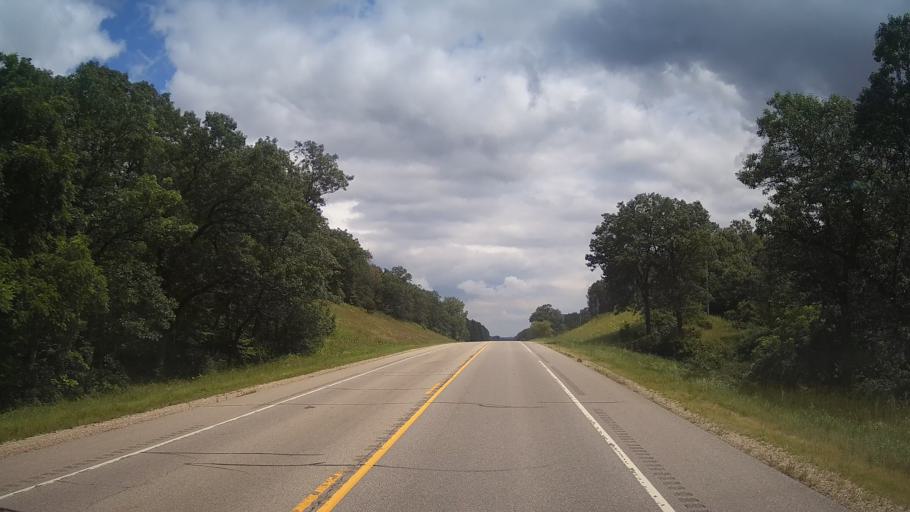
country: US
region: Wisconsin
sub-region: Marquette County
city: Westfield
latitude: 44.0218
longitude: -89.5594
